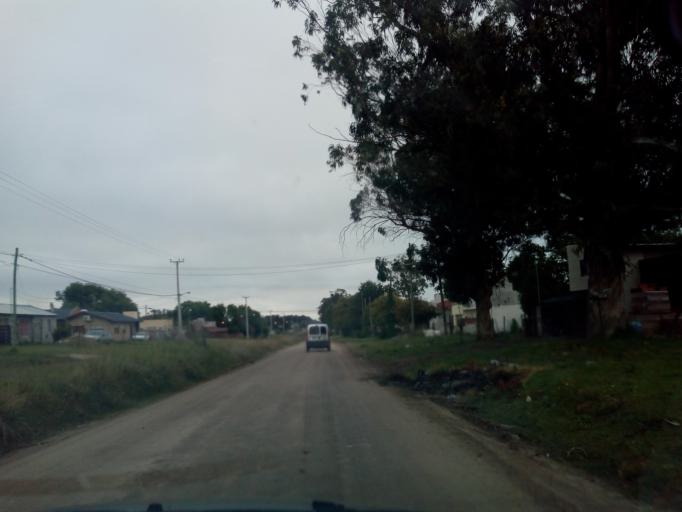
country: AR
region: Buenos Aires
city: Mar del Plata
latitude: -38.0669
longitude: -57.5689
